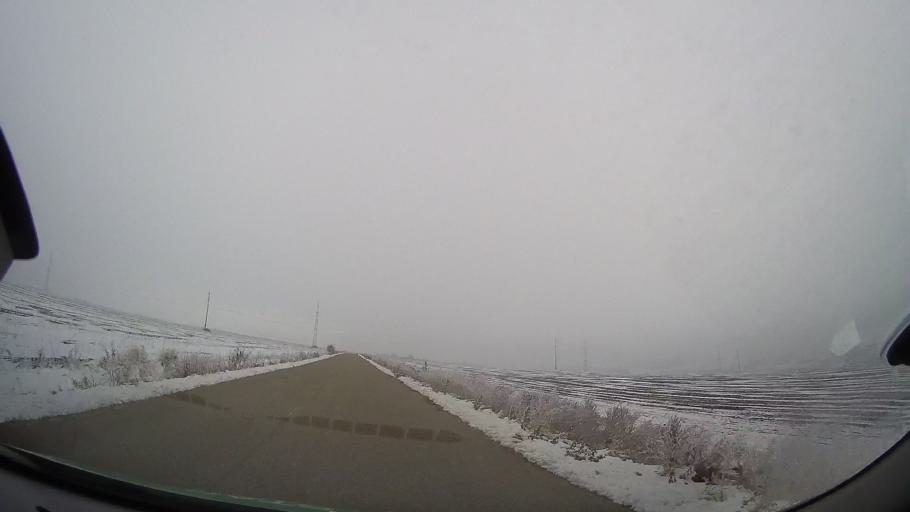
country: RO
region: Vaslui
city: Coroiesti
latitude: 46.2332
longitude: 27.4777
